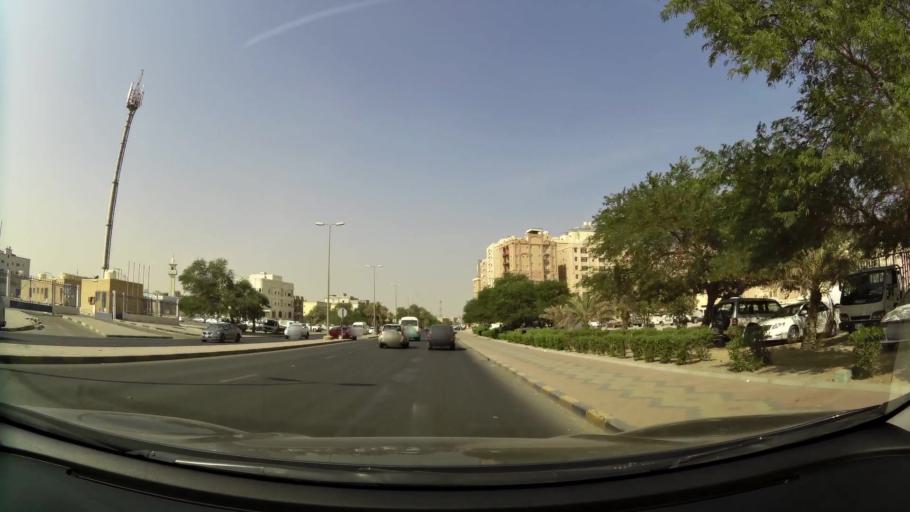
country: KW
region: Al Ahmadi
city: Al Fahahil
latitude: 29.0794
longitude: 48.1237
